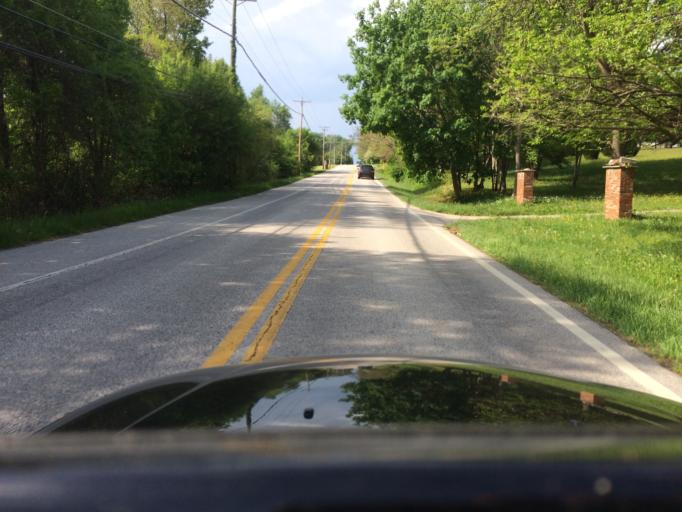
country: US
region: Maryland
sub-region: Howard County
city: Highland
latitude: 39.2477
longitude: -76.9835
